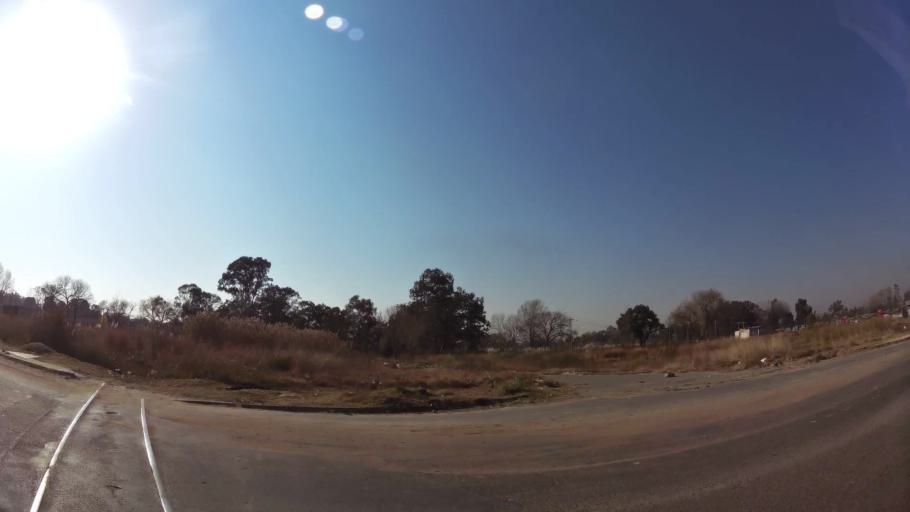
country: ZA
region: Gauteng
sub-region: Ekurhuleni Metropolitan Municipality
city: Boksburg
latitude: -26.2200
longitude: 28.2311
